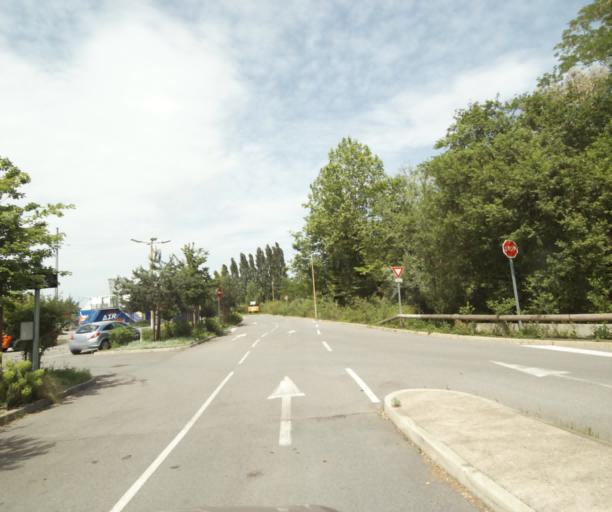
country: FR
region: Aquitaine
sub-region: Departement des Pyrenees-Atlantiques
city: Mouguerre
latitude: 43.4825
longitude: -1.4451
